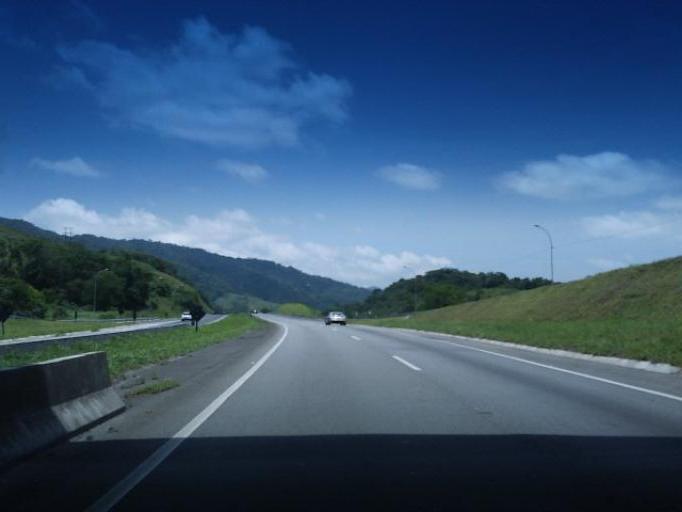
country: BR
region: Sao Paulo
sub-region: Miracatu
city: Miracatu
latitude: -24.2953
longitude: -47.4803
